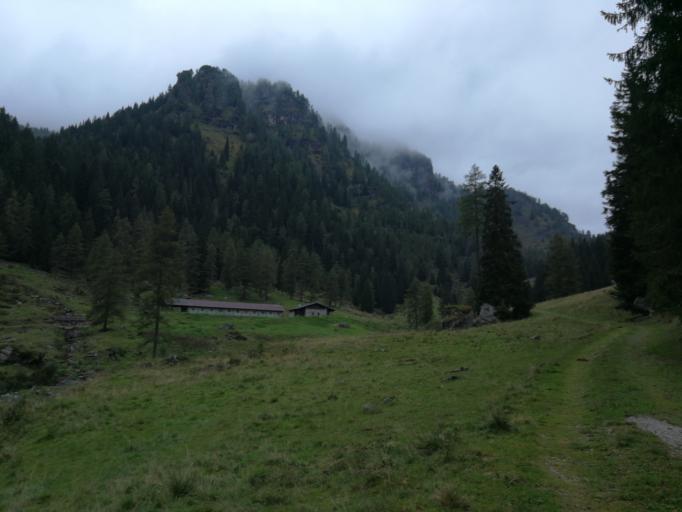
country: IT
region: Trentino-Alto Adige
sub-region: Provincia di Trento
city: Brione
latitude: 45.9120
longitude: 10.5318
